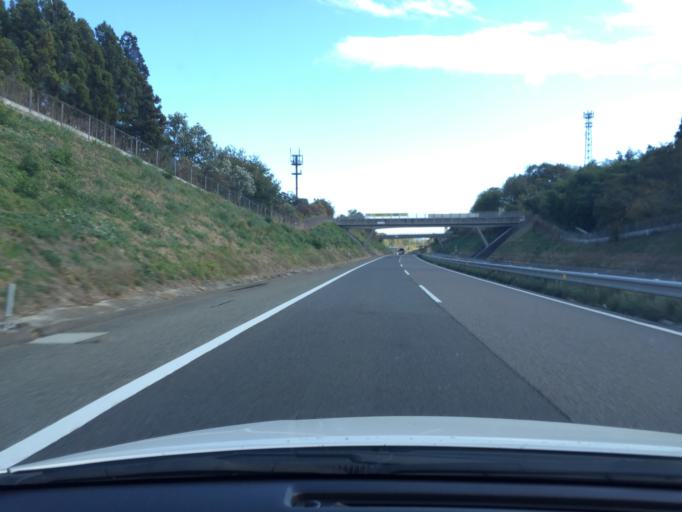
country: JP
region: Fukushima
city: Koriyama
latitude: 37.4491
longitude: 140.4126
